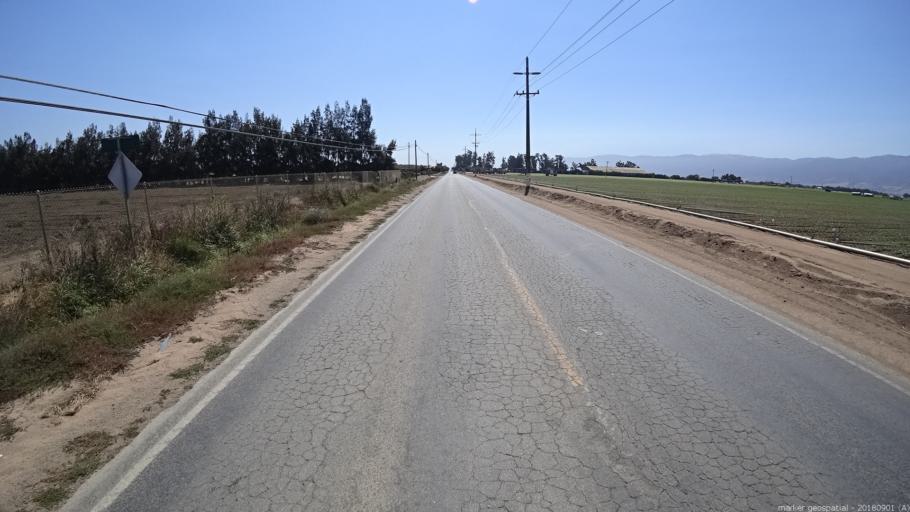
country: US
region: California
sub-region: Monterey County
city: Chualar
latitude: 36.6229
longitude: -121.5275
